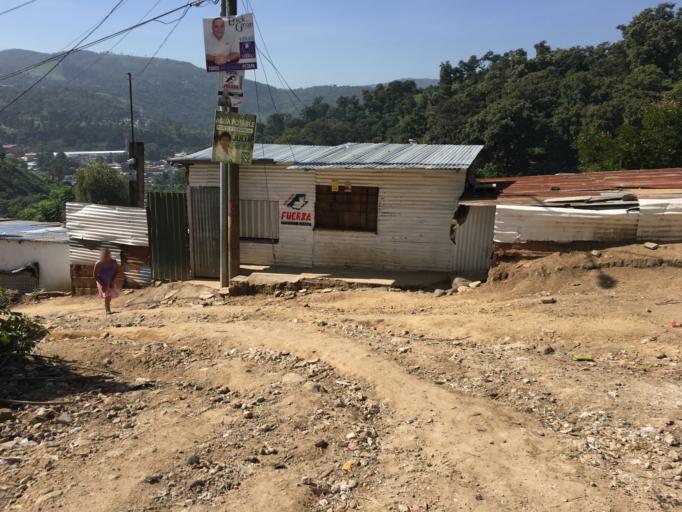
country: GT
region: Guatemala
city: Villa Canales
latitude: 14.4846
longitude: -90.5409
